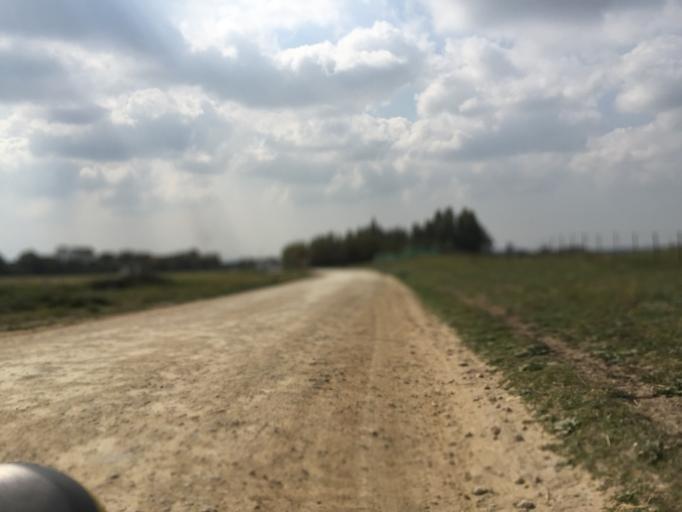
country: ES
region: Andalusia
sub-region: Provincia de Cadiz
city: Benalup-Casas Viejas
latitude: 36.3251
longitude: -5.8842
